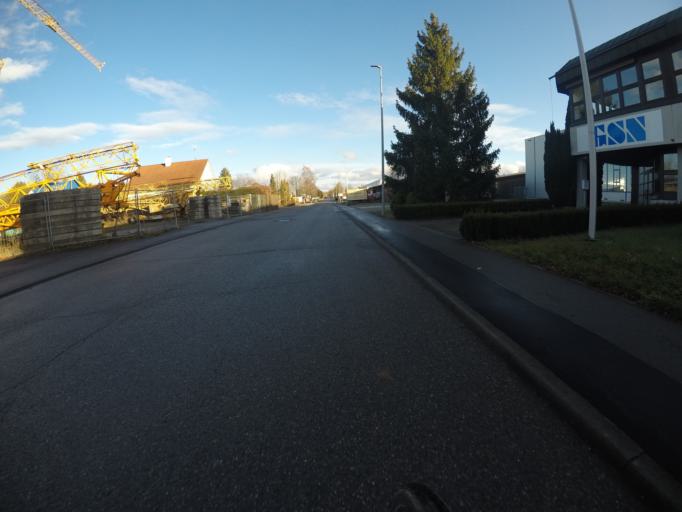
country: DE
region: Baden-Wuerttemberg
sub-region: Regierungsbezirk Stuttgart
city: Bondorf
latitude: 48.5282
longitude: 8.8745
